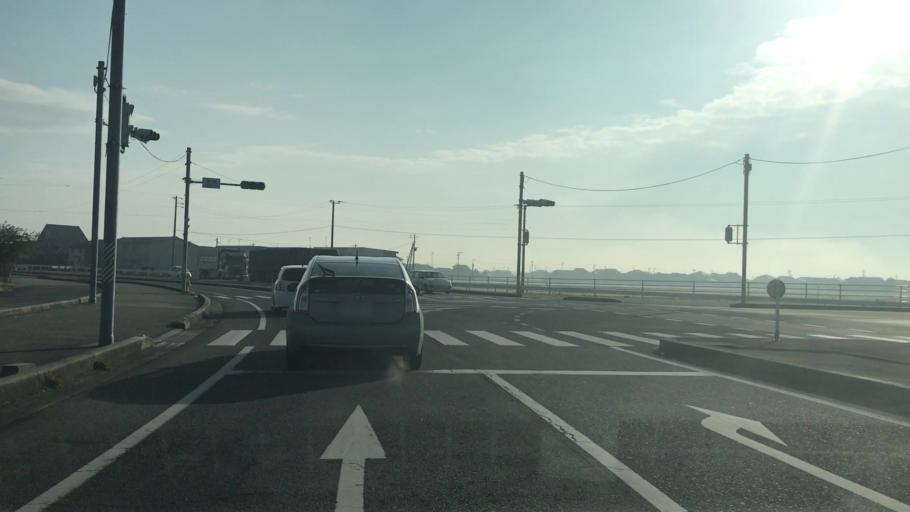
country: JP
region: Saga Prefecture
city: Saga-shi
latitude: 33.2176
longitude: 130.1711
